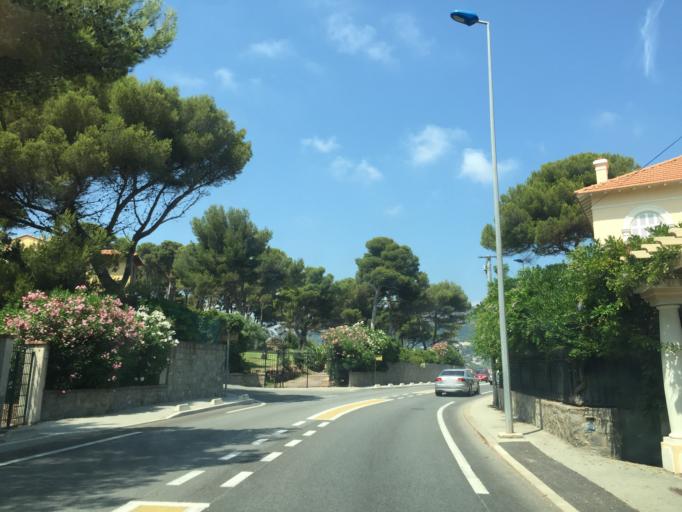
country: FR
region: Provence-Alpes-Cote d'Azur
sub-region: Departement du Var
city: Saint-Raphael
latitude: 43.4222
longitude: 6.8573
